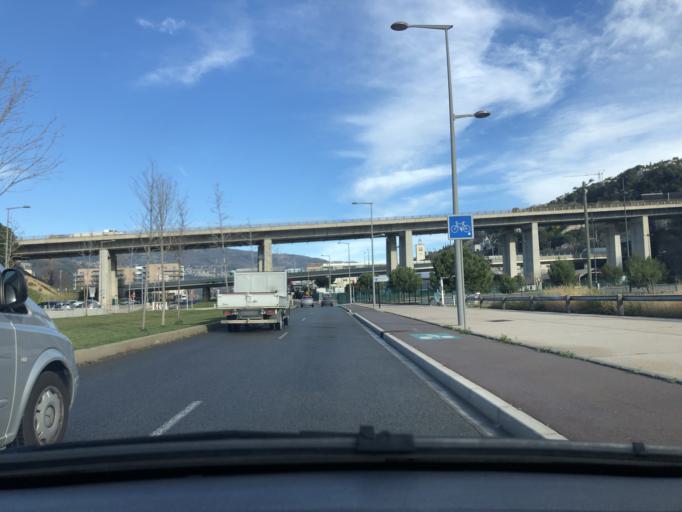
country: FR
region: Provence-Alpes-Cote d'Azur
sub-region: Departement des Alpes-Maritimes
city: Saint-Laurent-du-Var
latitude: 43.7078
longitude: 7.1961
